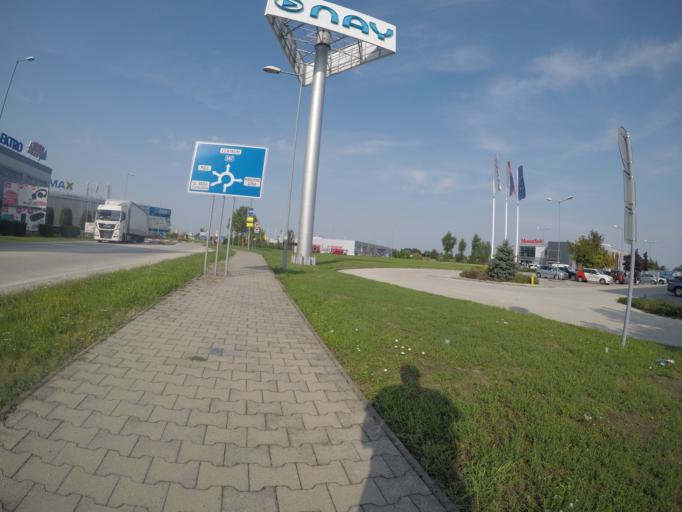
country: SK
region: Trnavsky
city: Dunajska Streda
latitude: 47.9969
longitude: 17.6324
